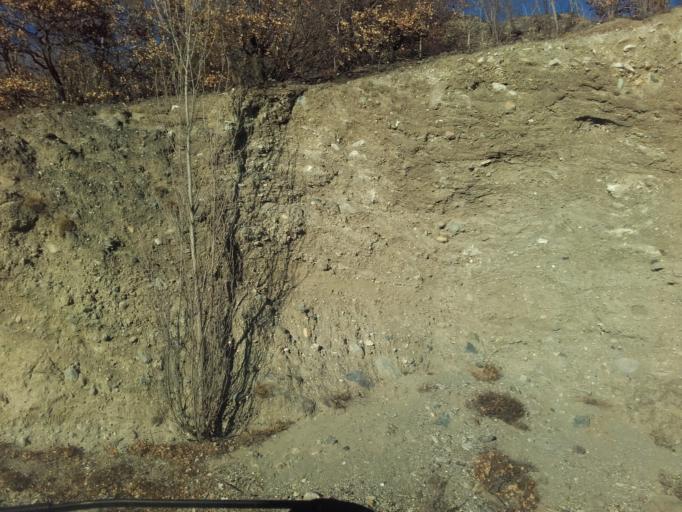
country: IT
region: Piedmont
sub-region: Provincia di Torino
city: Bussoleno
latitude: 45.1504
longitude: 7.1395
